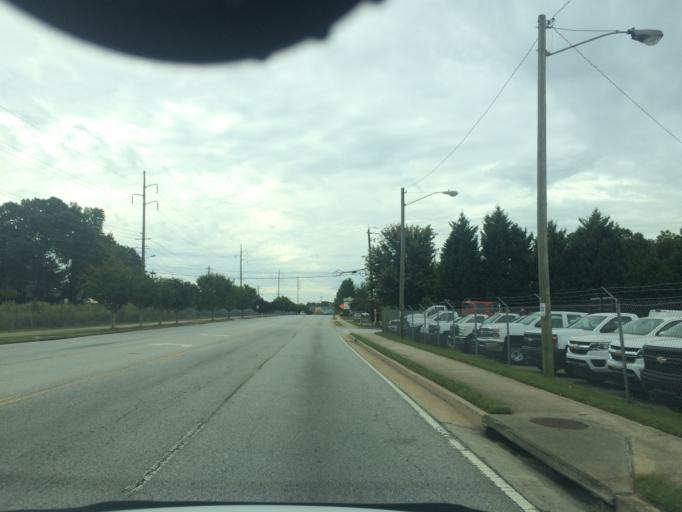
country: US
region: Georgia
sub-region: Cobb County
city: Smyrna
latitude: 33.9001
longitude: -84.5234
